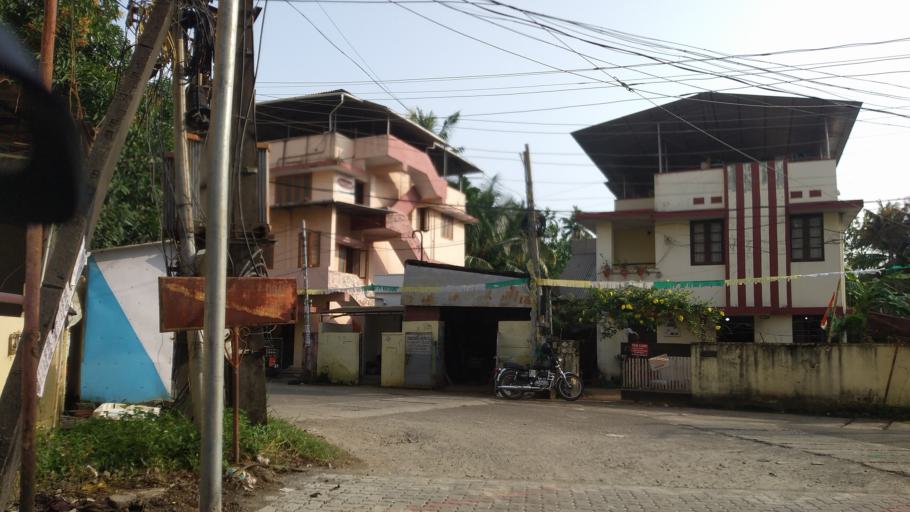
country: IN
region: Kerala
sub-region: Ernakulam
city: Cochin
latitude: 9.9863
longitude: 76.2893
